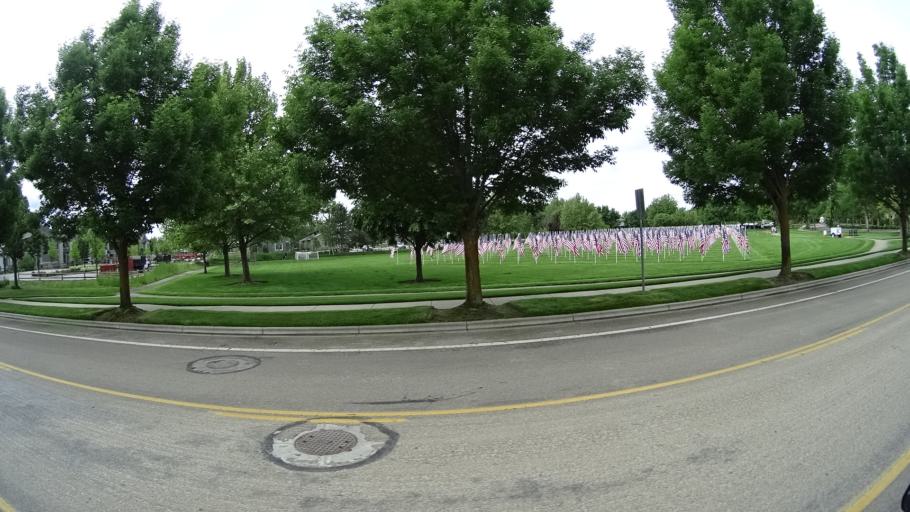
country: US
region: Idaho
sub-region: Ada County
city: Eagle
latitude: 43.6887
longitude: -116.3445
